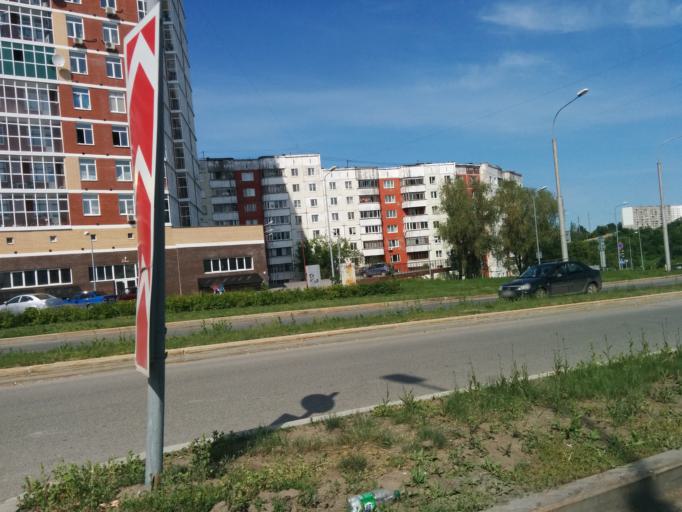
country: RU
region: Perm
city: Perm
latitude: 58.0050
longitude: 56.3100
